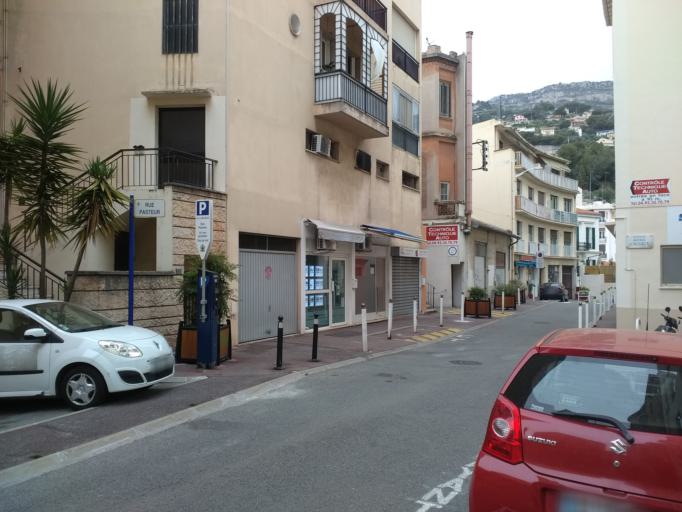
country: MC
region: Commune de Monaco
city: Moneghetti
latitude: 43.7382
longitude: 7.4176
